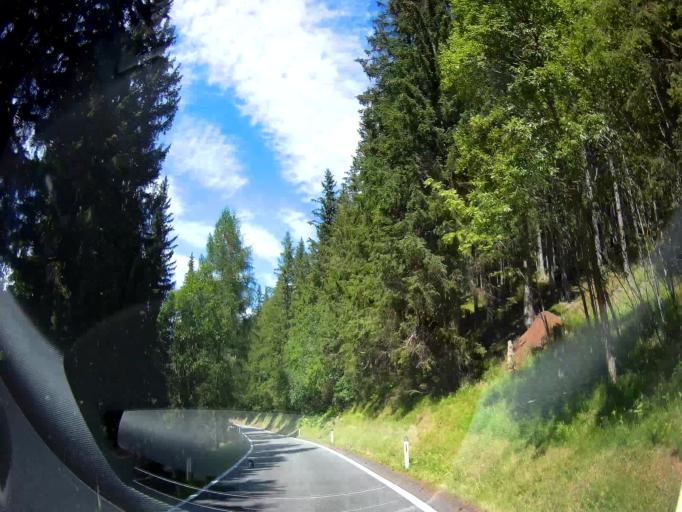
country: AT
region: Carinthia
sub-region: Politischer Bezirk Sankt Veit an der Glan
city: Glodnitz
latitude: 46.9241
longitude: 14.0546
